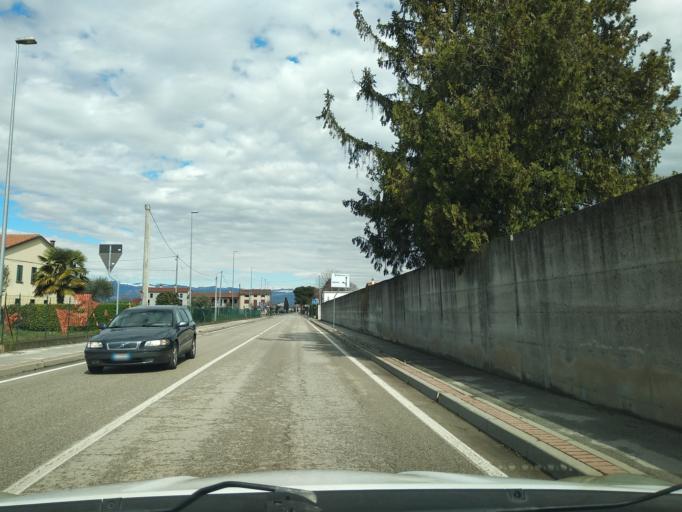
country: IT
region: Veneto
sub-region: Provincia di Vicenza
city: Monticello Conte Otto
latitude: 45.5897
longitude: 11.5794
